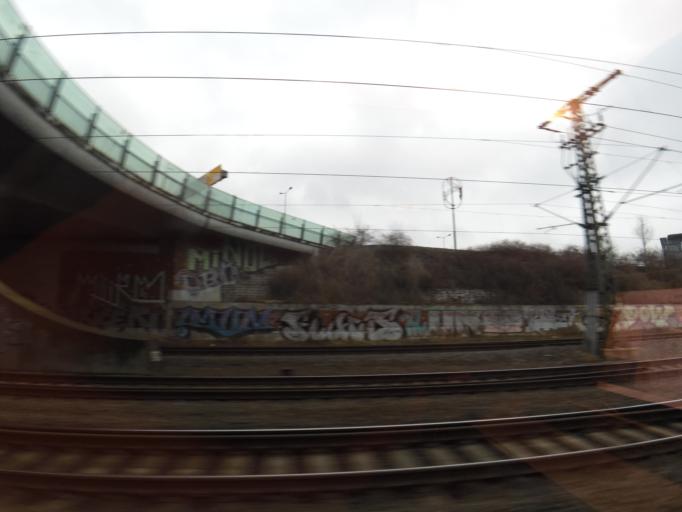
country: DE
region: Saxony
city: Leipzig
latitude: 51.3624
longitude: 12.4003
